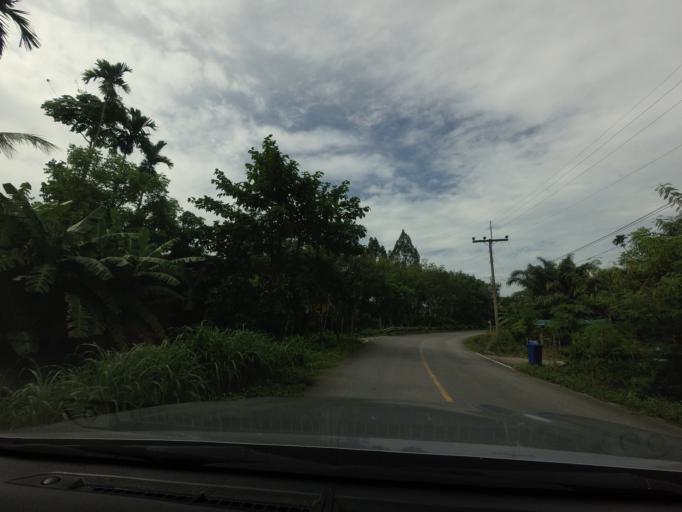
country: TH
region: Nakhon Si Thammarat
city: Phra Phrom
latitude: 8.2833
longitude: 99.9141
